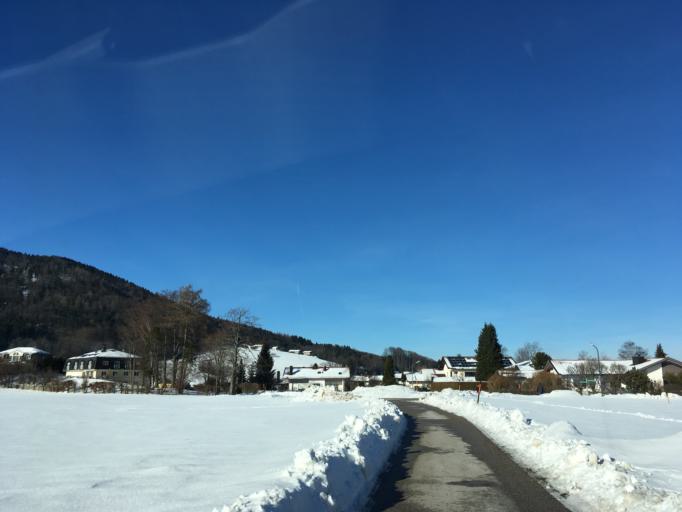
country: DE
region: Bavaria
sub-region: Upper Bavaria
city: Aschau im Chiemgau
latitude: 47.7798
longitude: 12.3194
